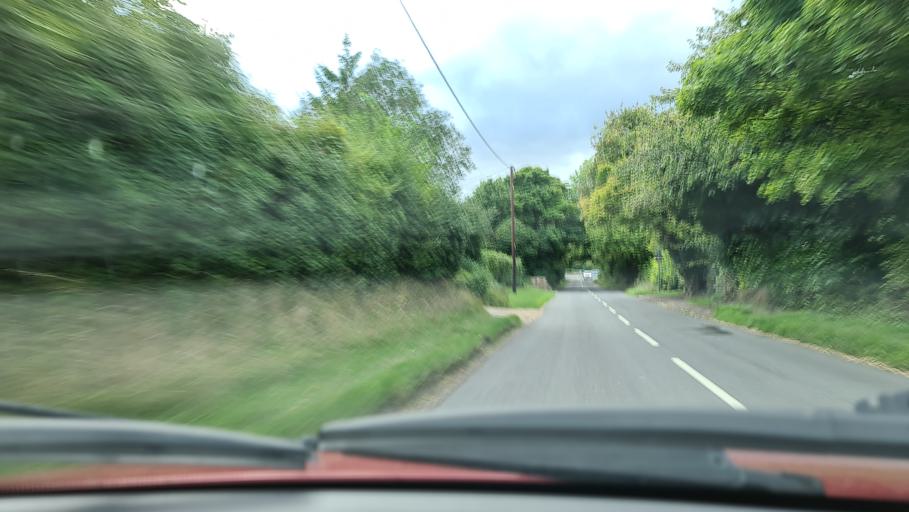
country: GB
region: England
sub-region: Buckinghamshire
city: Princes Risborough
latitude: 51.7380
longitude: -0.8132
